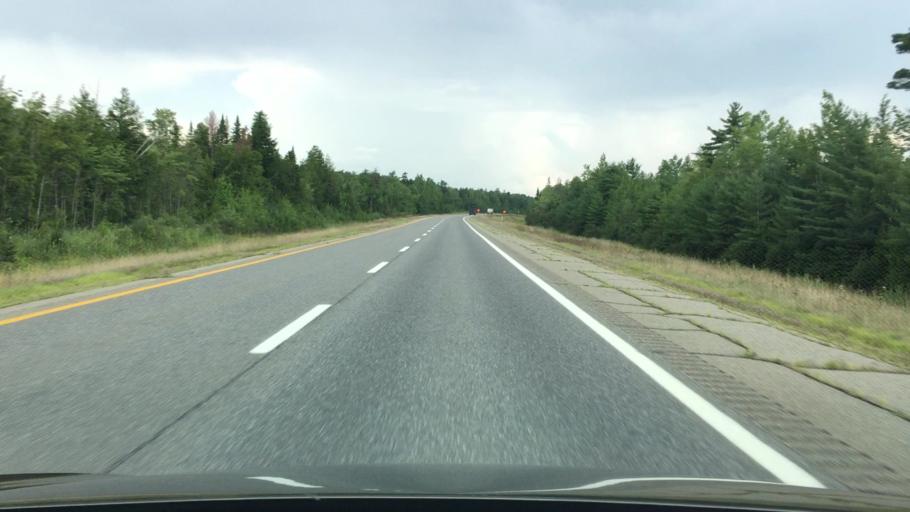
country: US
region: Maine
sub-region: Penobscot County
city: Medway
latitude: 45.5436
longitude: -68.5519
